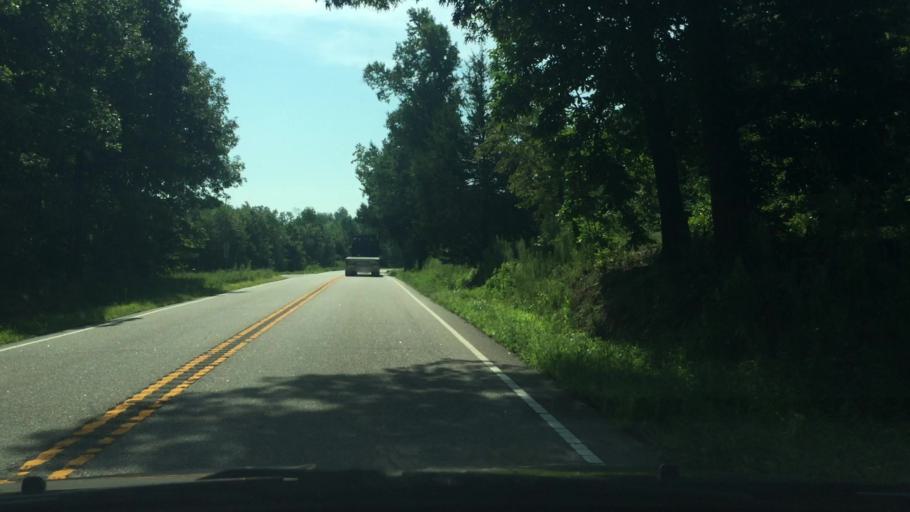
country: US
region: Virginia
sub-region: Sussex County
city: Sussex
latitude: 37.0125
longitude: -77.2761
